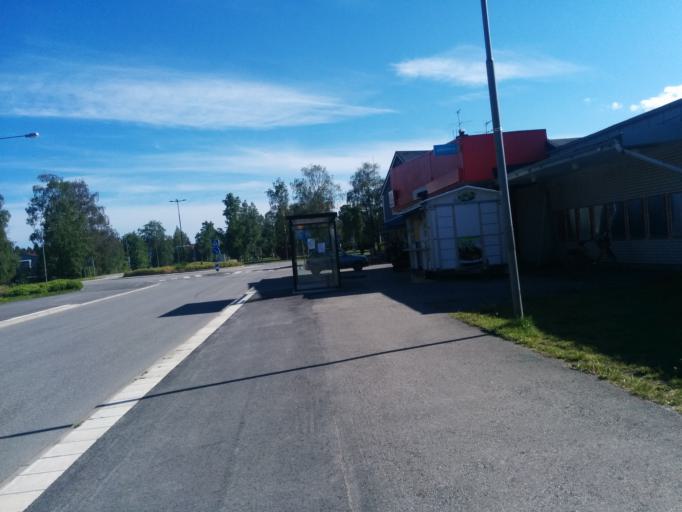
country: SE
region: Vaesterbotten
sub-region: Umea Kommun
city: Hoernefors
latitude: 63.6238
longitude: 19.9082
